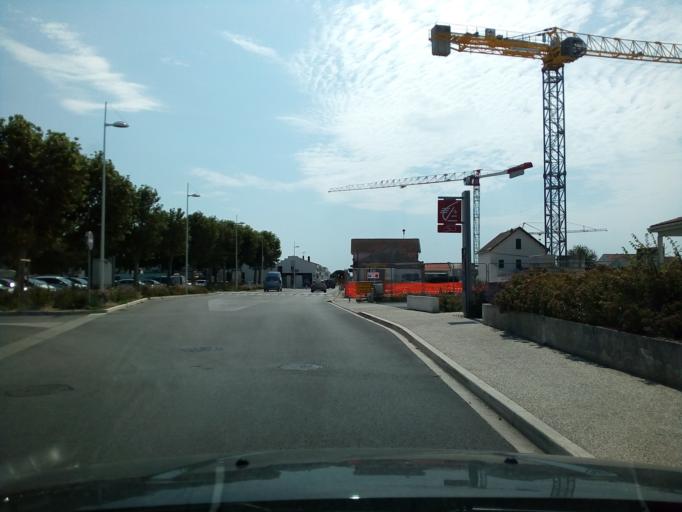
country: FR
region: Poitou-Charentes
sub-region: Departement de la Charente-Maritime
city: Dolus-d'Oleron
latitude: 45.9413
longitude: -1.3086
